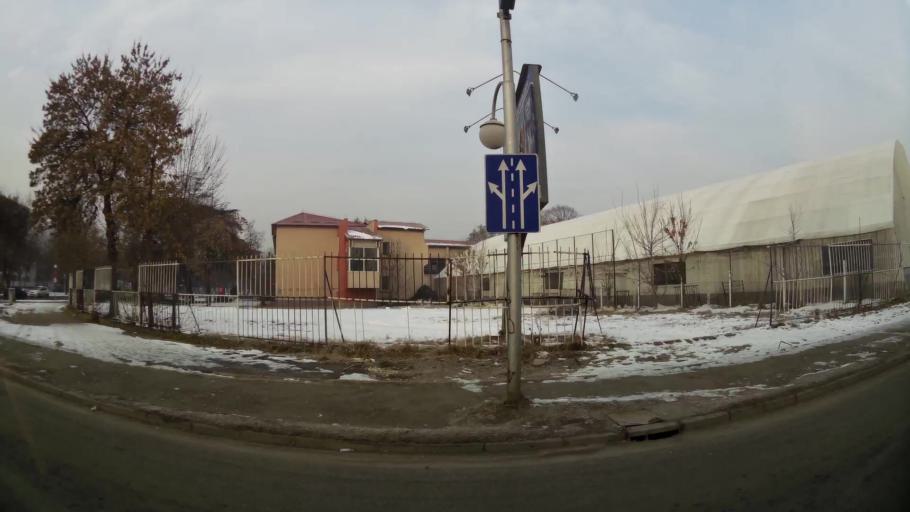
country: MK
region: Cair
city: Cair
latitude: 42.0218
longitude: 21.4438
